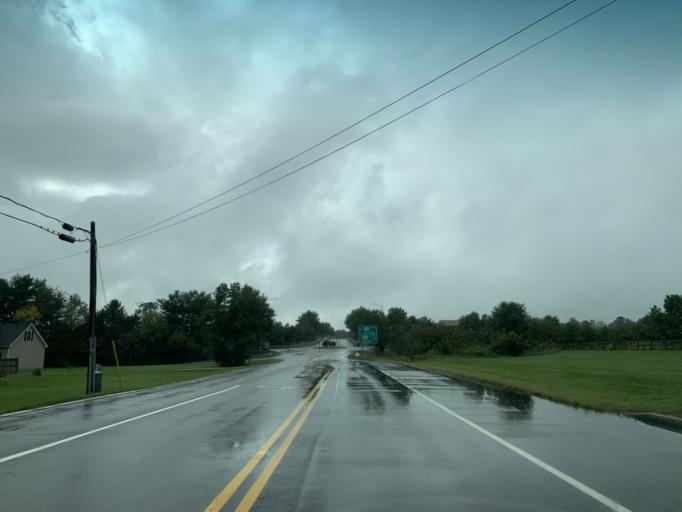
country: US
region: Maryland
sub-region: Queen Anne's County
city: Kingstown
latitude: 39.2636
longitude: -75.8610
